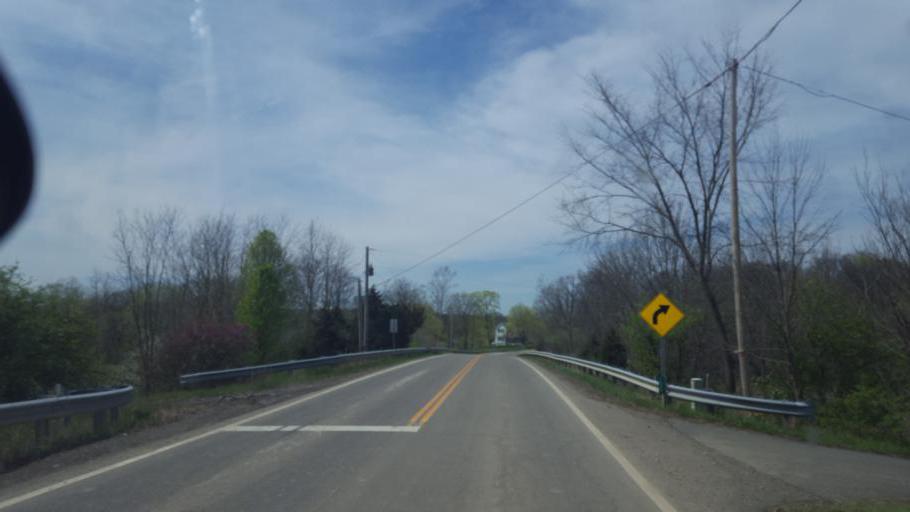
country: US
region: Ohio
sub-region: Ashland County
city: Ashland
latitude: 40.8230
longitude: -82.3947
